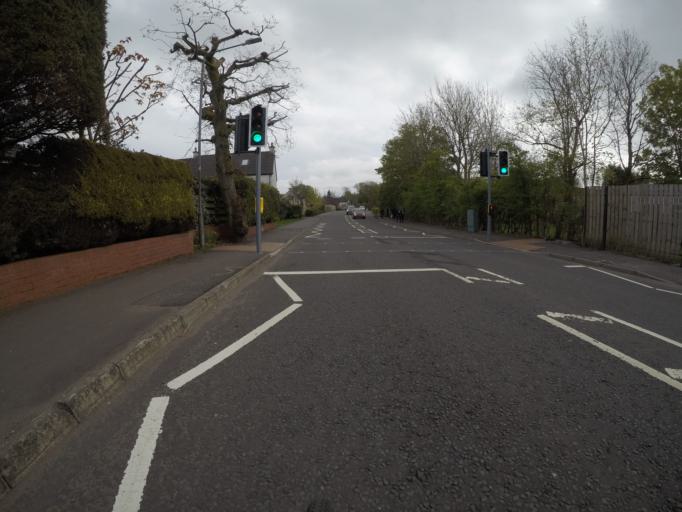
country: GB
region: Scotland
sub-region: East Renfrewshire
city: Newton Mearns
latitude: 55.7769
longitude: -4.3061
